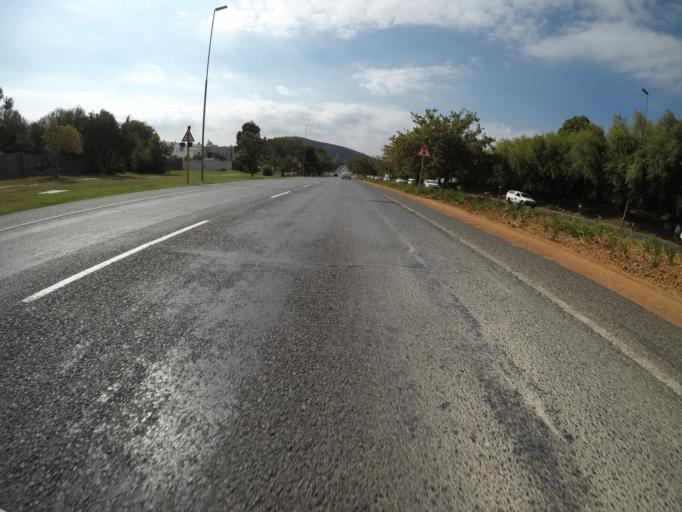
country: ZA
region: Western Cape
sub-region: Cape Winelands District Municipality
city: Stellenbosch
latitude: -33.9506
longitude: 18.8549
